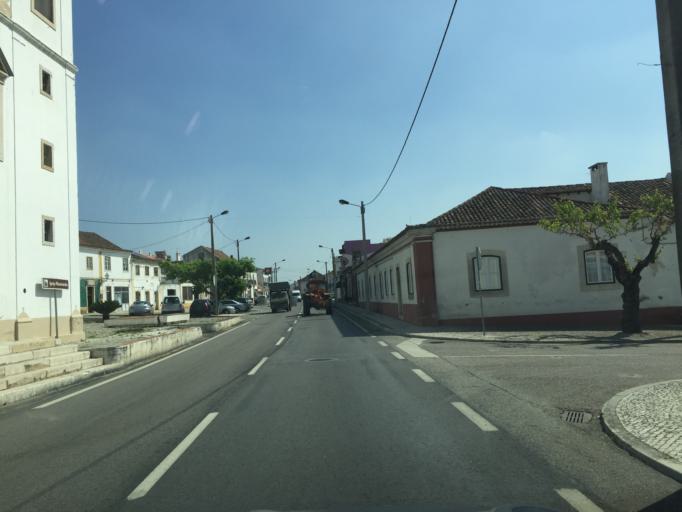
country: PT
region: Santarem
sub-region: Golega
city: Golega
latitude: 39.3559
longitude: -8.4835
